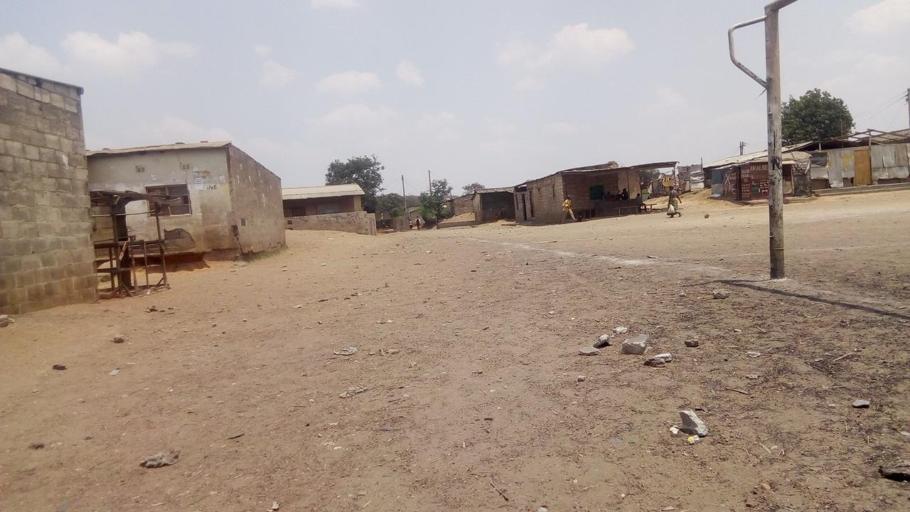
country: ZM
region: Lusaka
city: Lusaka
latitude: -15.3633
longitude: 28.2946
